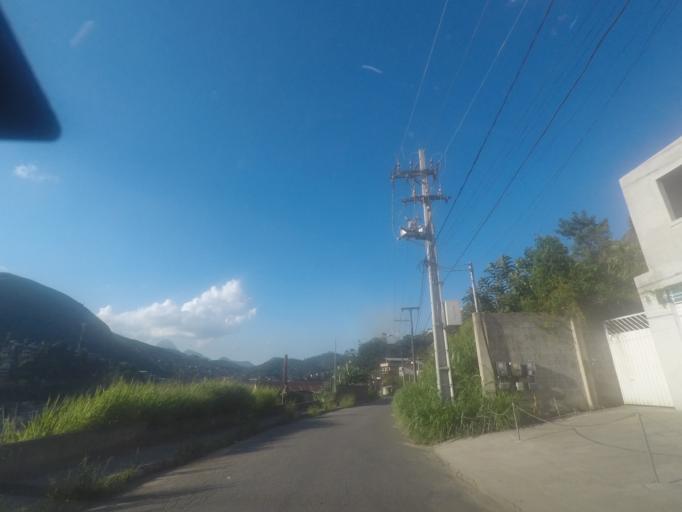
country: BR
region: Rio de Janeiro
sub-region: Petropolis
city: Petropolis
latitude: -22.4910
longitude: -43.1509
